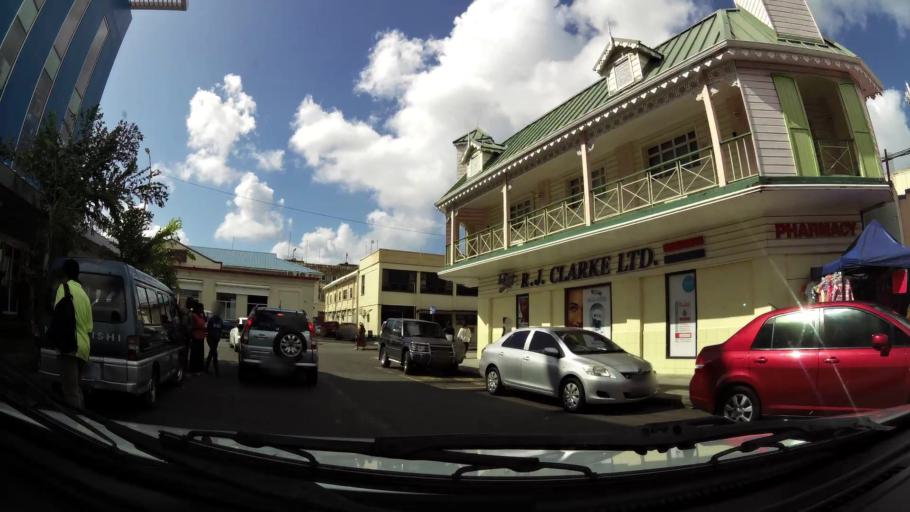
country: LC
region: Castries Quarter
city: Castries
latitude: 14.0101
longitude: -60.9914
